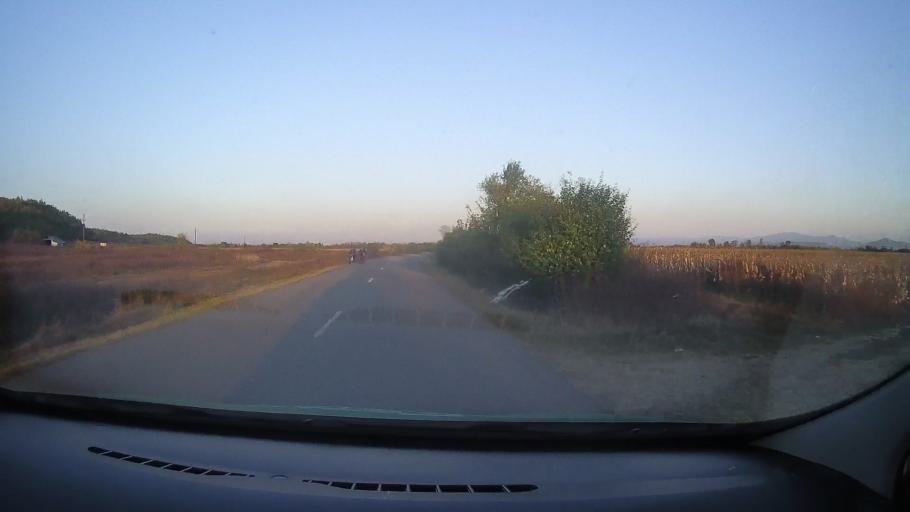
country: RO
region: Timis
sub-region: Comuna Manastiur
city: Manastiur
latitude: 45.8358
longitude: 22.0222
